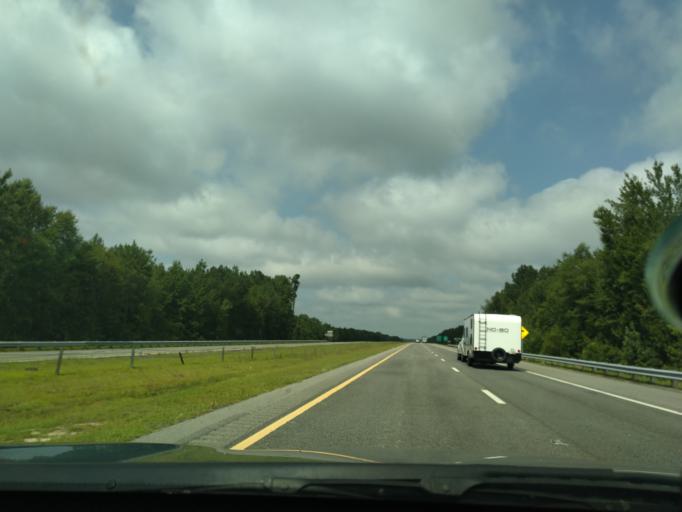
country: US
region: North Carolina
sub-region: Pitt County
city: Bethel
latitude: 35.8320
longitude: -77.3454
